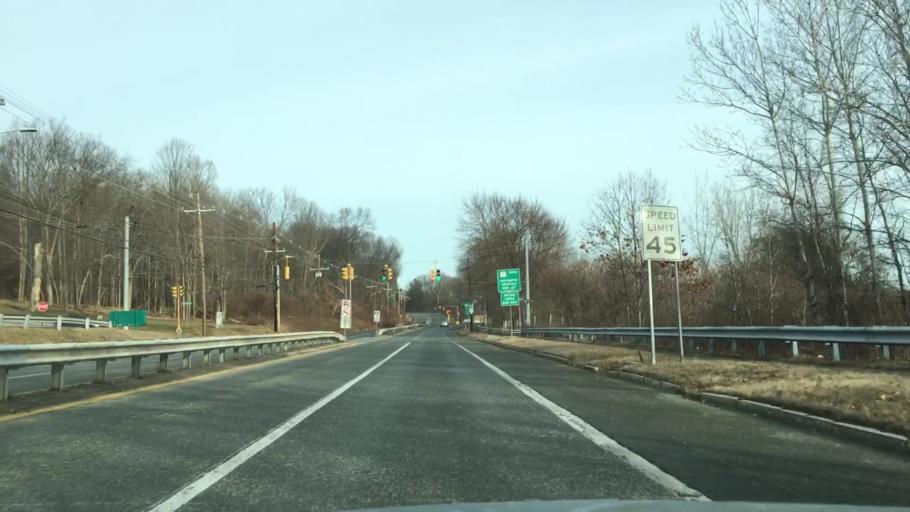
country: US
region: Massachusetts
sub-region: Hampden County
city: Chicopee
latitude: 42.1671
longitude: -72.6326
